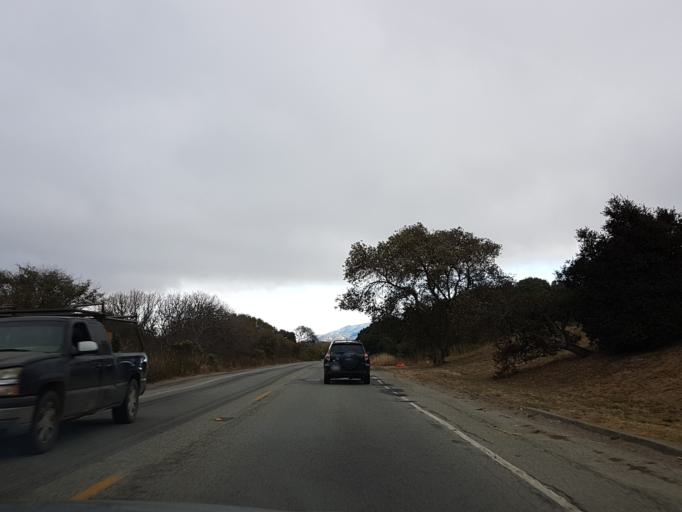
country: US
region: California
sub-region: Monterey County
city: Salinas
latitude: 36.6132
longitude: -121.6551
